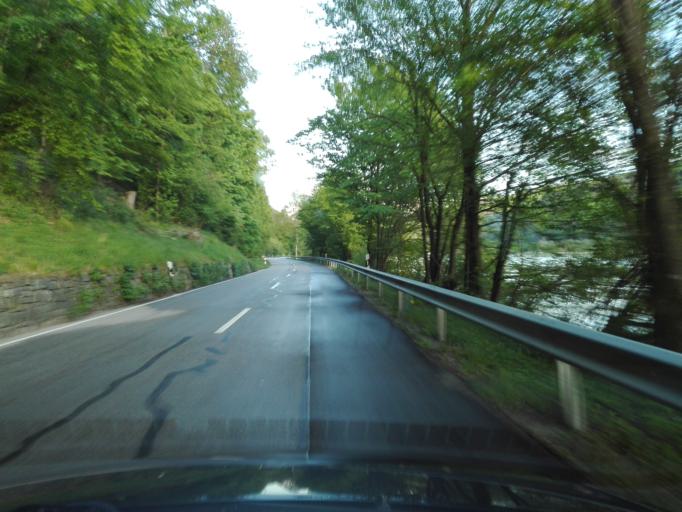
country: DE
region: Bavaria
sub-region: Lower Bavaria
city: Untergriesbach
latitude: 48.5286
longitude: 13.6883
